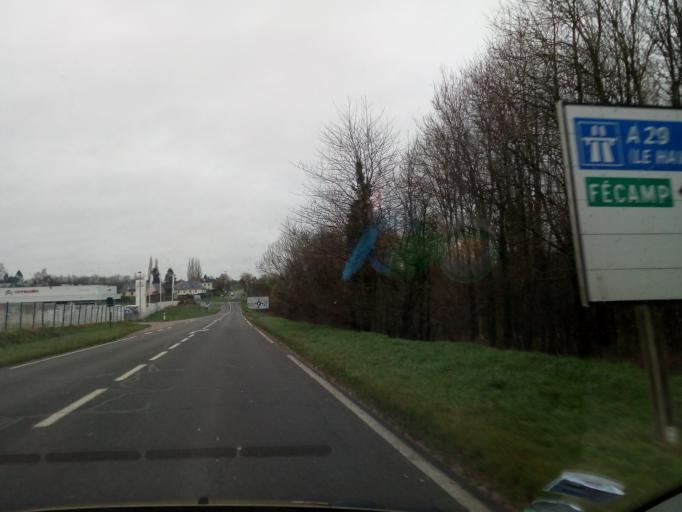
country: FR
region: Haute-Normandie
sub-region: Departement de la Seine-Maritime
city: Auzebosc
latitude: 49.6042
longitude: 0.7401
